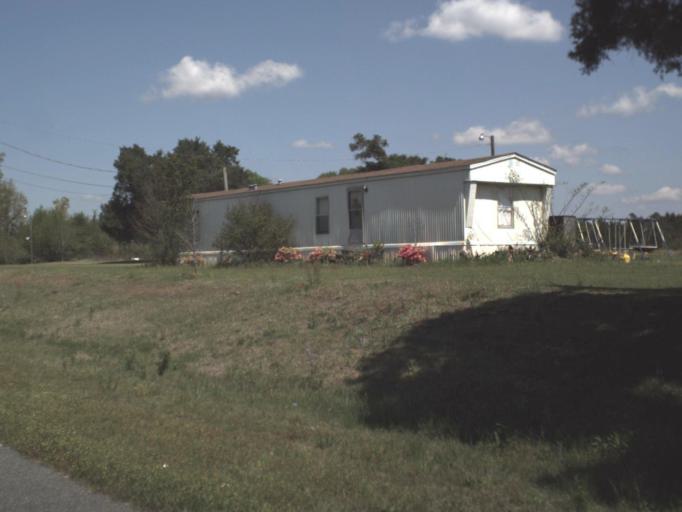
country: US
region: Florida
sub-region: Escambia County
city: Century
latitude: 30.9526
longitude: -87.2012
